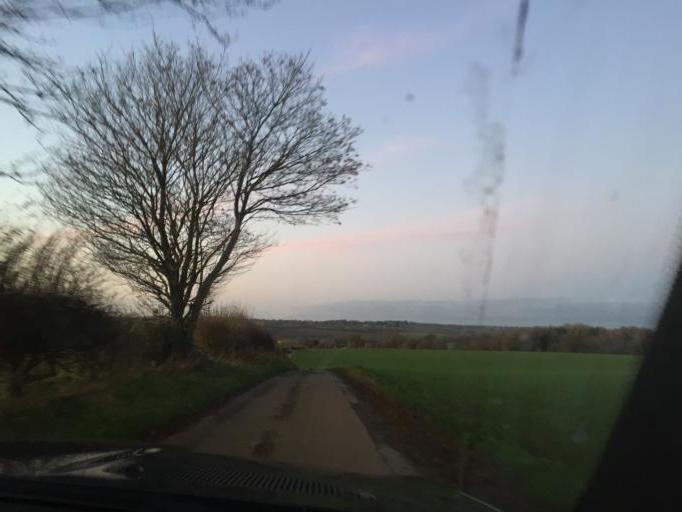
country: GB
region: England
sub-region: Northamptonshire
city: Brackley
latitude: 52.0900
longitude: -1.1109
